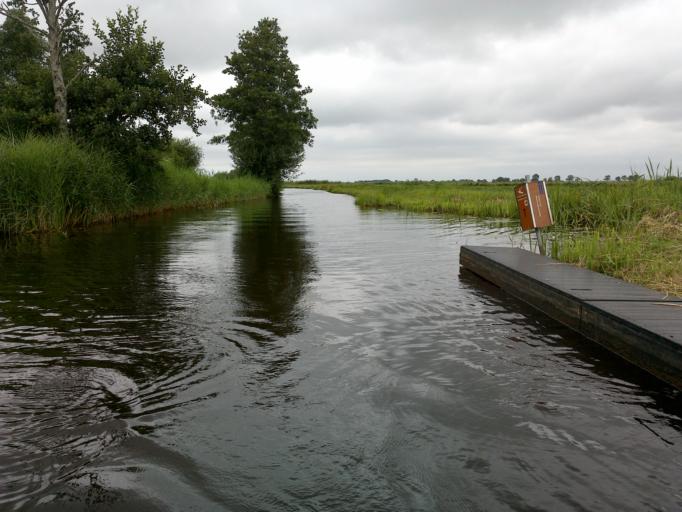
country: NL
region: Overijssel
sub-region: Gemeente Steenwijkerland
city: Giethoorn
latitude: 52.7388
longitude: 6.1083
